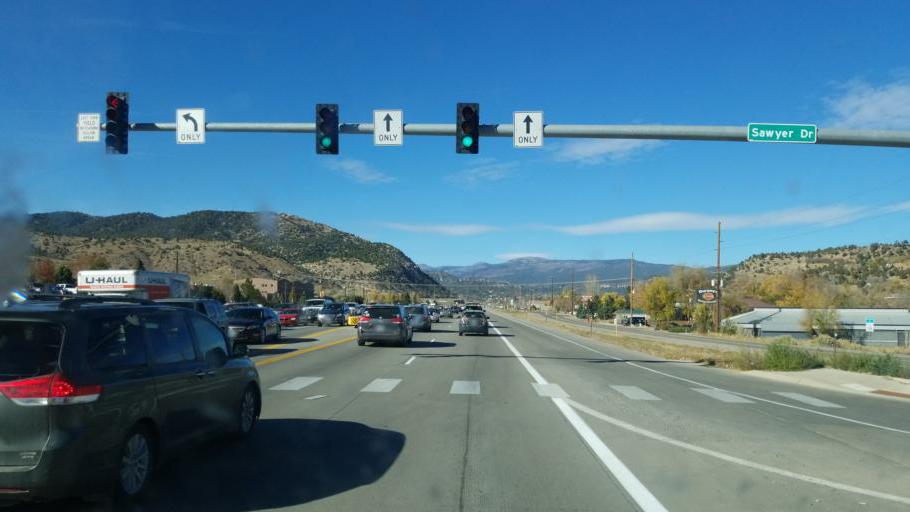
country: US
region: Colorado
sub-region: La Plata County
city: Durango
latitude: 37.2420
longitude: -107.8716
